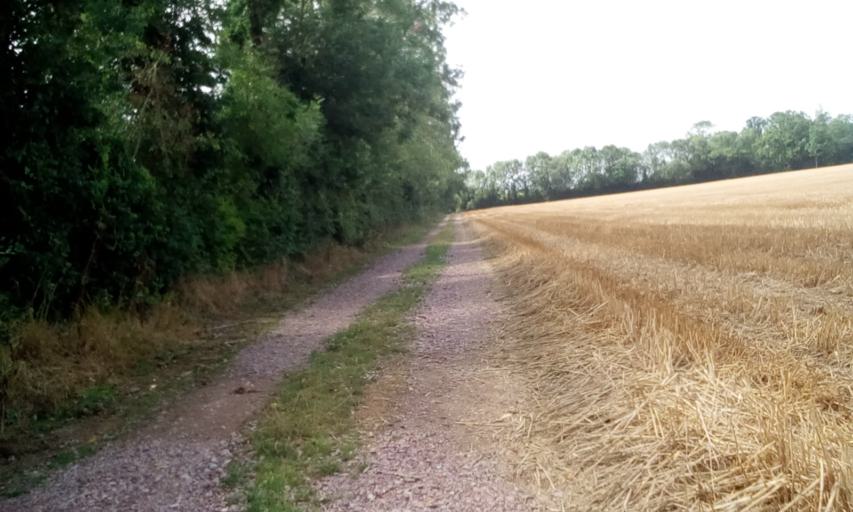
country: FR
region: Lower Normandy
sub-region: Departement du Calvados
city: Cheux
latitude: 49.1857
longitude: -0.5317
